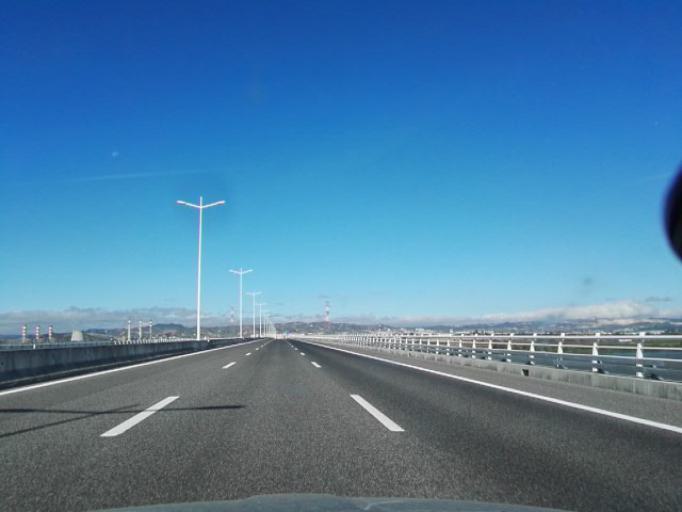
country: PT
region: Lisbon
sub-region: Vila Franca de Xira
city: Castanheira do Ribatejo
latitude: 39.0119
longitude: -8.9310
